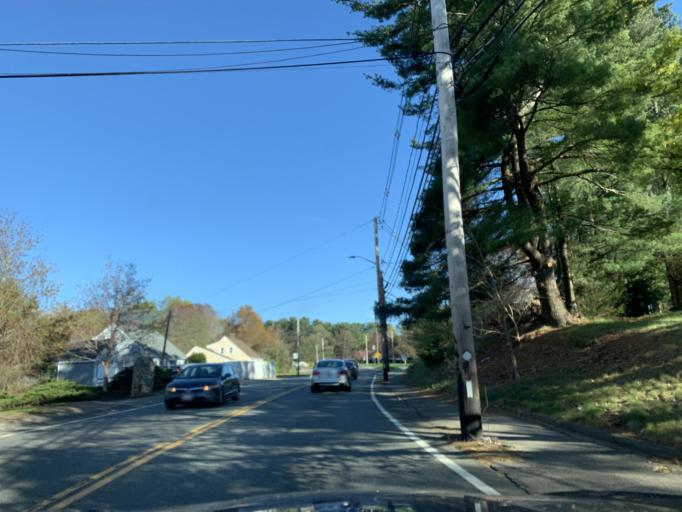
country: US
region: Massachusetts
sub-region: Norfolk County
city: Canton
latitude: 42.1332
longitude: -71.1369
